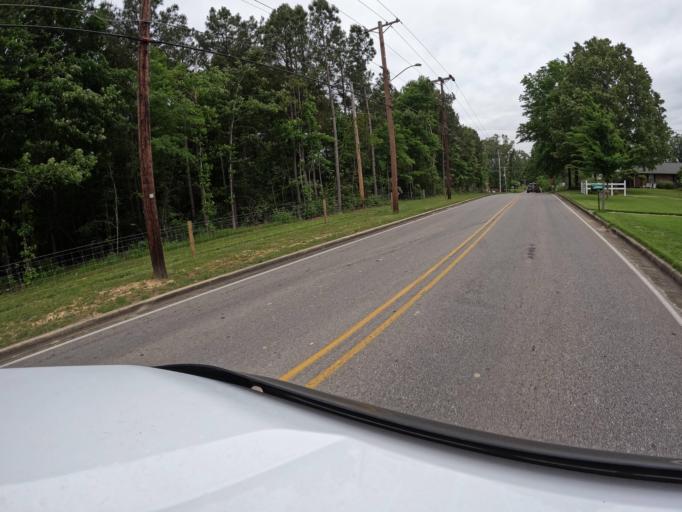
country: US
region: Mississippi
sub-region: Lee County
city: Tupelo
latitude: 34.2709
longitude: -88.7377
